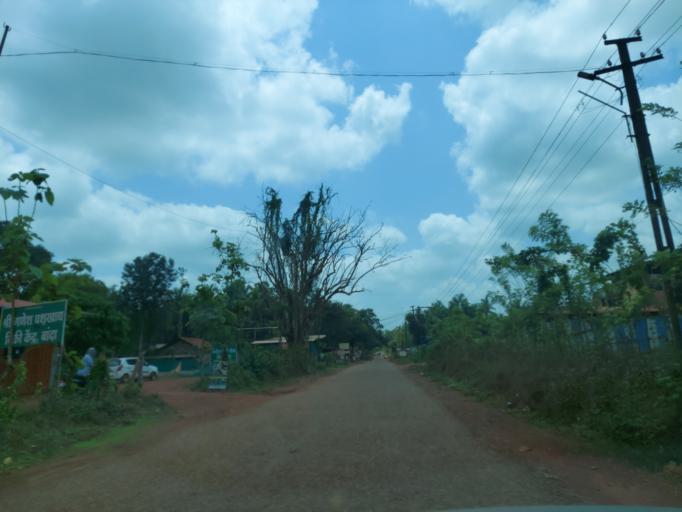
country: IN
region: Maharashtra
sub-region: Sindhudurg
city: Savantvadi
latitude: 15.8199
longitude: 73.8694
